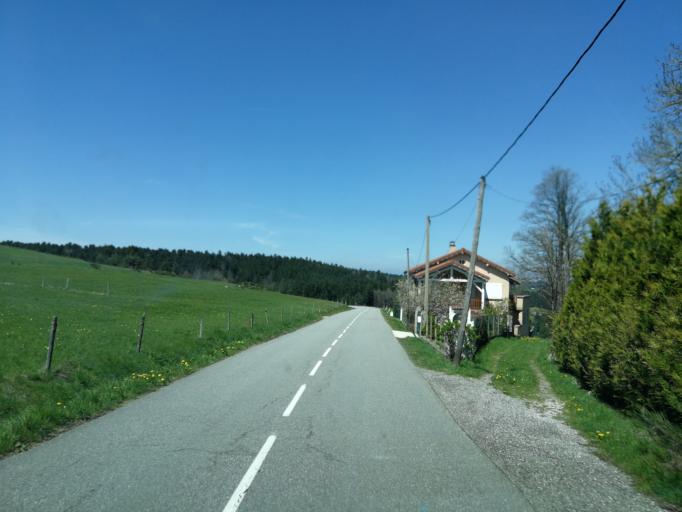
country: FR
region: Rhone-Alpes
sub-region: Departement de la Loire
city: Marlhes
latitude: 45.2859
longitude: 4.3897
